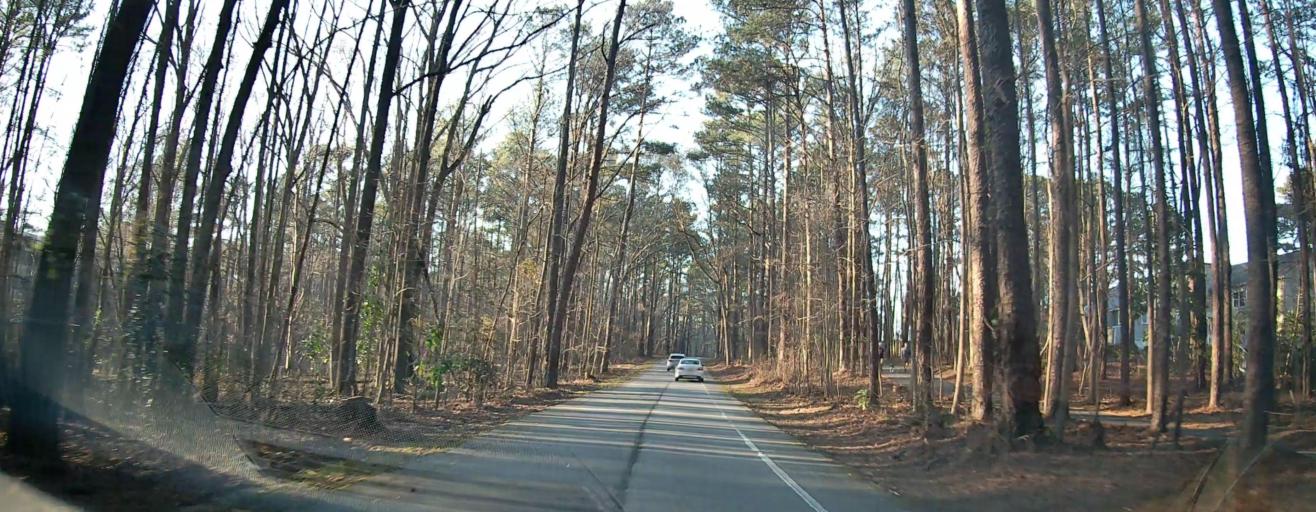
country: US
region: Georgia
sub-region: Fayette County
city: Peachtree City
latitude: 33.4024
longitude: -84.5888
